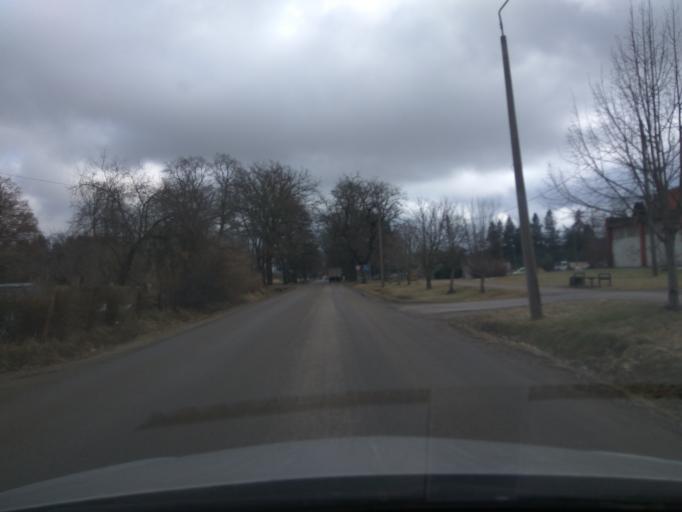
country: LV
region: Kuldigas Rajons
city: Kuldiga
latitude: 57.2771
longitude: 22.0200
